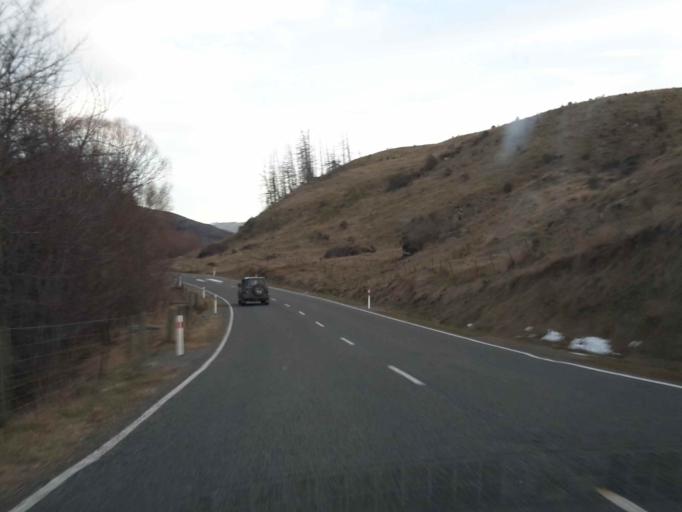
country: NZ
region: Canterbury
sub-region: Timaru District
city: Pleasant Point
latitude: -44.0557
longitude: 170.6761
